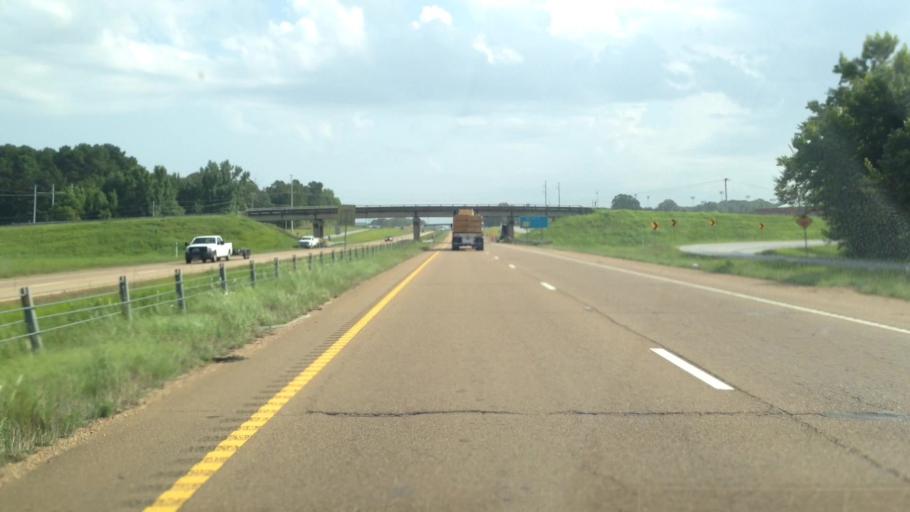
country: US
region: Mississippi
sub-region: Hinds County
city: Terry
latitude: 32.0919
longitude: -90.3074
